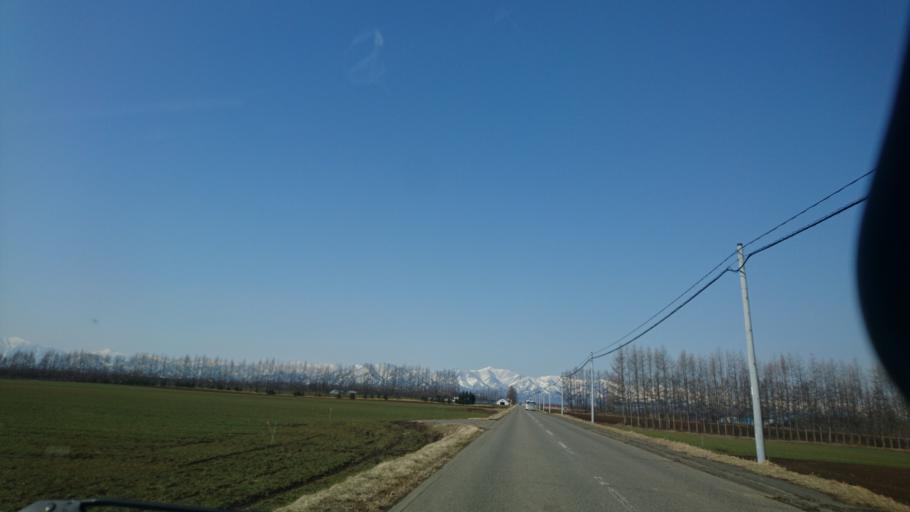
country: JP
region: Hokkaido
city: Obihiro
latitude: 42.9046
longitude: 143.1023
